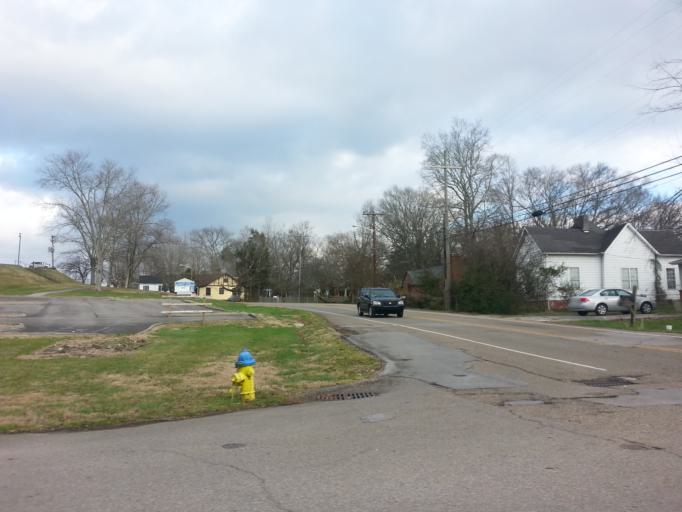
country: US
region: Tennessee
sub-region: Knox County
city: Knoxville
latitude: 35.9564
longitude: -83.8806
